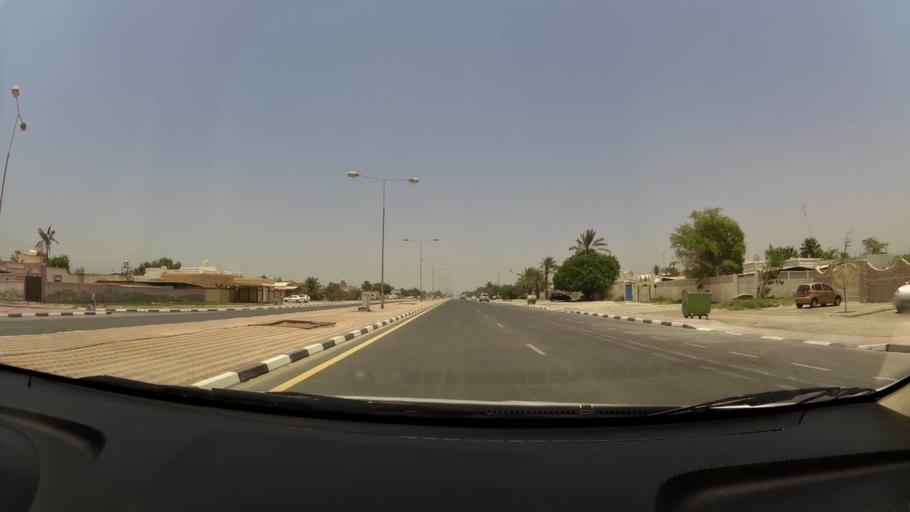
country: AE
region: Umm al Qaywayn
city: Umm al Qaywayn
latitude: 25.5545
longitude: 55.5551
